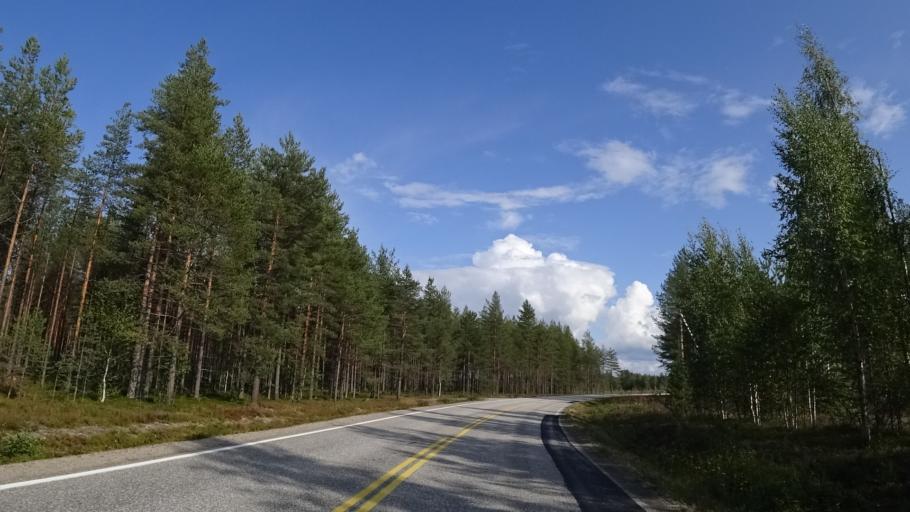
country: FI
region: North Karelia
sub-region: Pielisen Karjala
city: Lieksa
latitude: 63.4334
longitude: 30.0932
